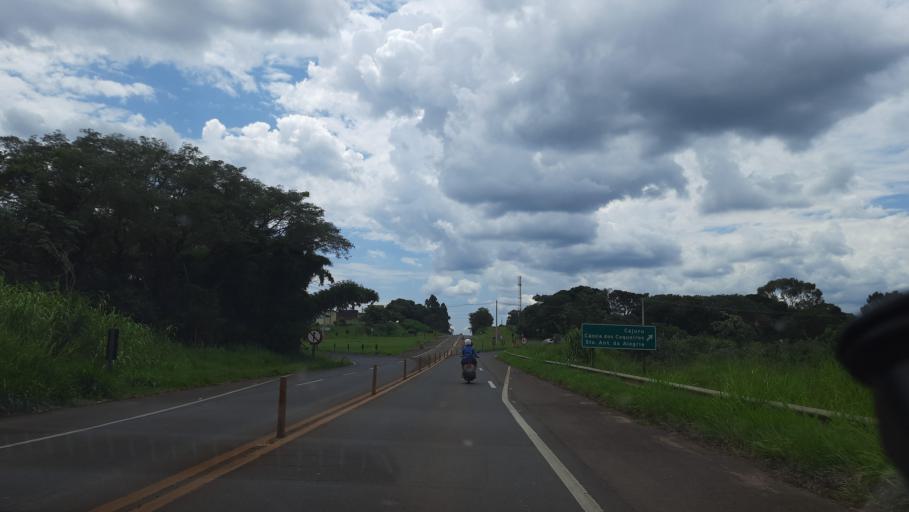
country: BR
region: Sao Paulo
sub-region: Cajuru
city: Cajuru
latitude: -21.2748
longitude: -47.2897
